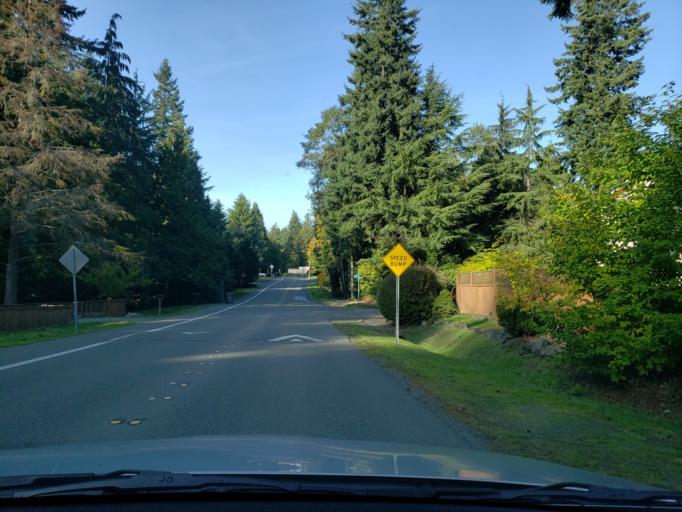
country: US
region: Washington
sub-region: Snohomish County
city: Meadowdale
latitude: 47.8651
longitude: -122.3145
